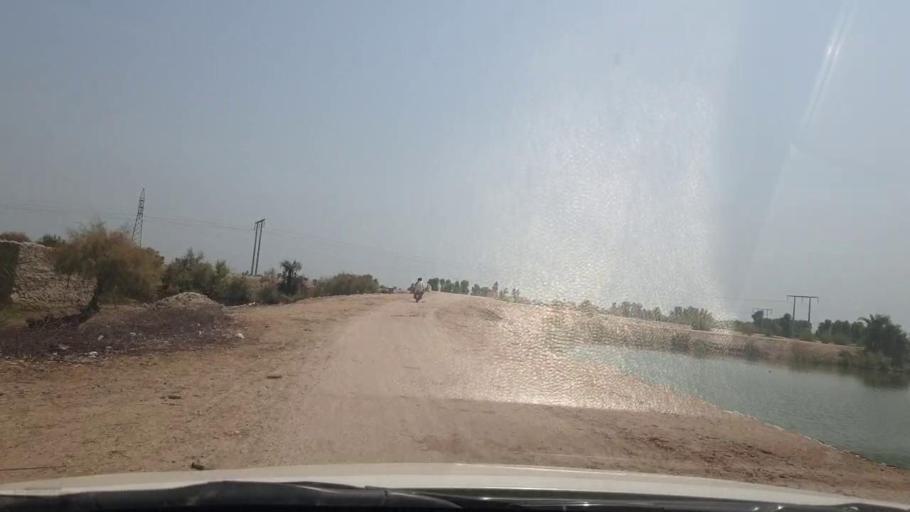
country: PK
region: Sindh
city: Rustam jo Goth
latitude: 28.0243
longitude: 68.8002
